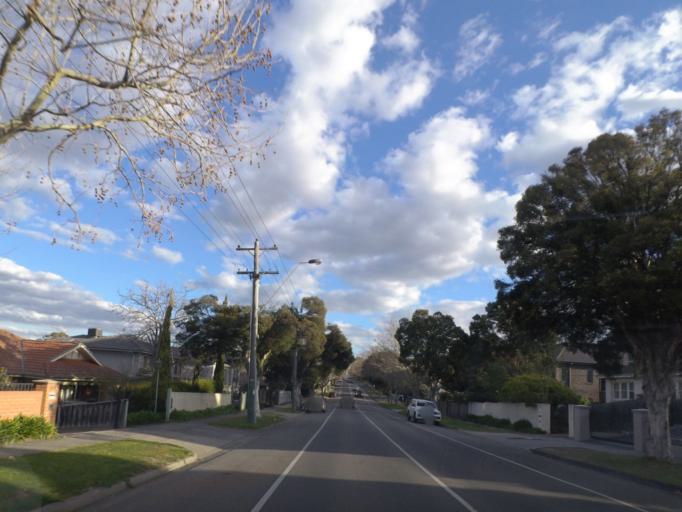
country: AU
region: Victoria
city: Mont Albert
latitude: -37.8070
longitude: 145.1010
